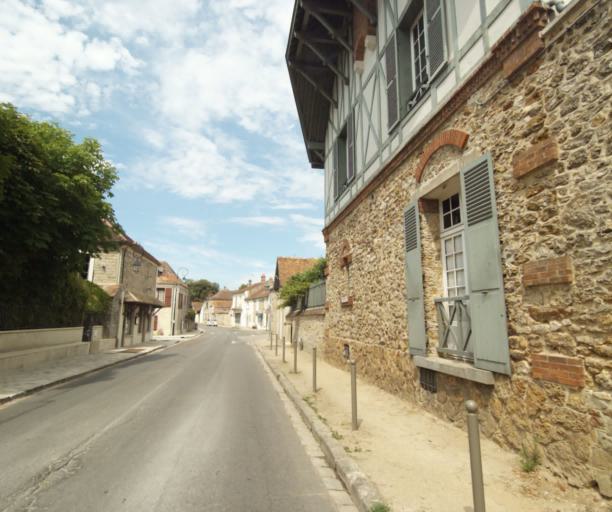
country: FR
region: Ile-de-France
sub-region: Departement de Seine-et-Marne
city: Barbizon
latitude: 48.4461
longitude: 2.6015
